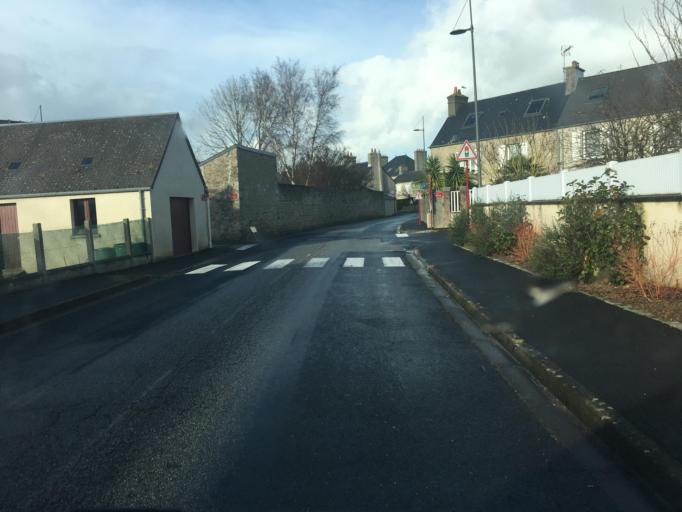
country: FR
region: Lower Normandy
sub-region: Departement de la Manche
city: Saint-Vaast-la-Hougue
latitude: 49.5870
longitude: -1.2730
